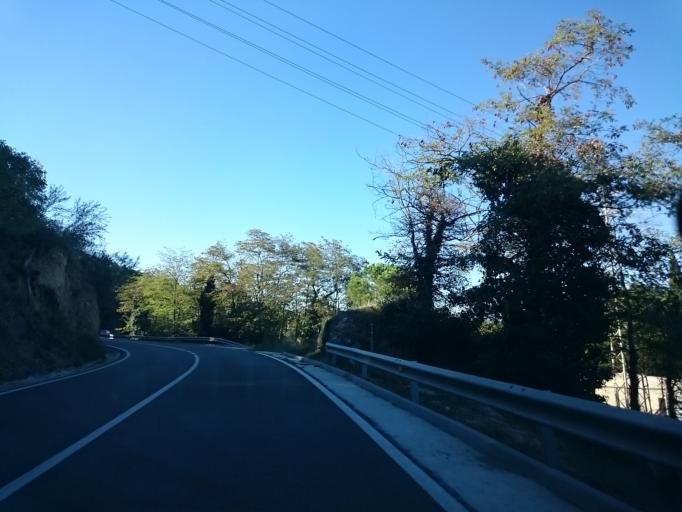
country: ES
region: Catalonia
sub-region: Provincia de Barcelona
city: Capellades
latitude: 41.5343
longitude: 1.6815
